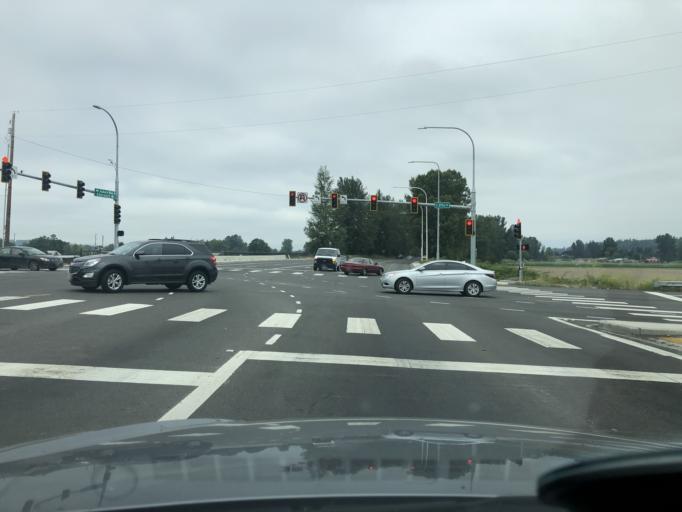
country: US
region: Washington
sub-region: King County
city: Kent
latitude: 47.3535
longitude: -122.2290
